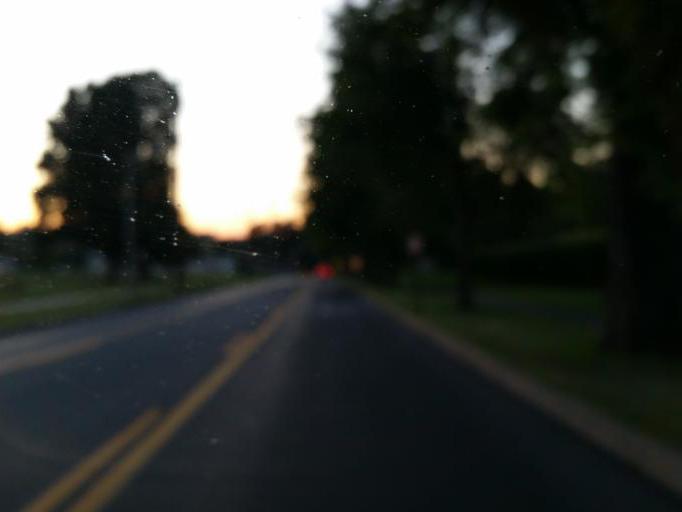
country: US
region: Pennsylvania
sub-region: Dauphin County
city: Hershey
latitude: 40.2821
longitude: -76.6414
